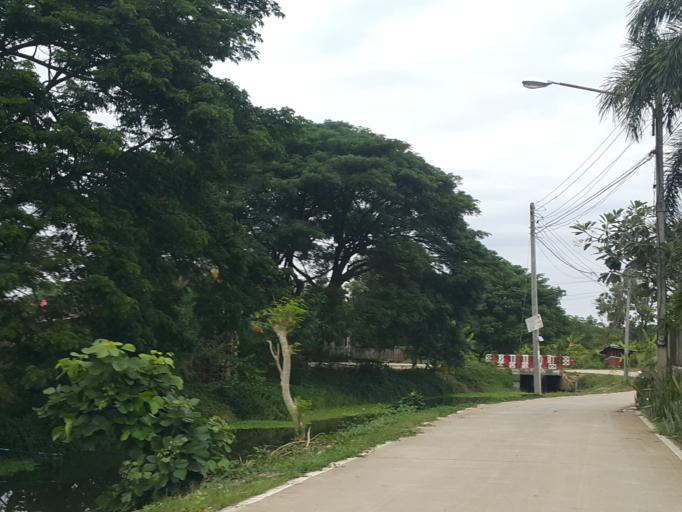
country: TH
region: Lampang
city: Lampang
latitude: 18.3062
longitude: 99.4991
